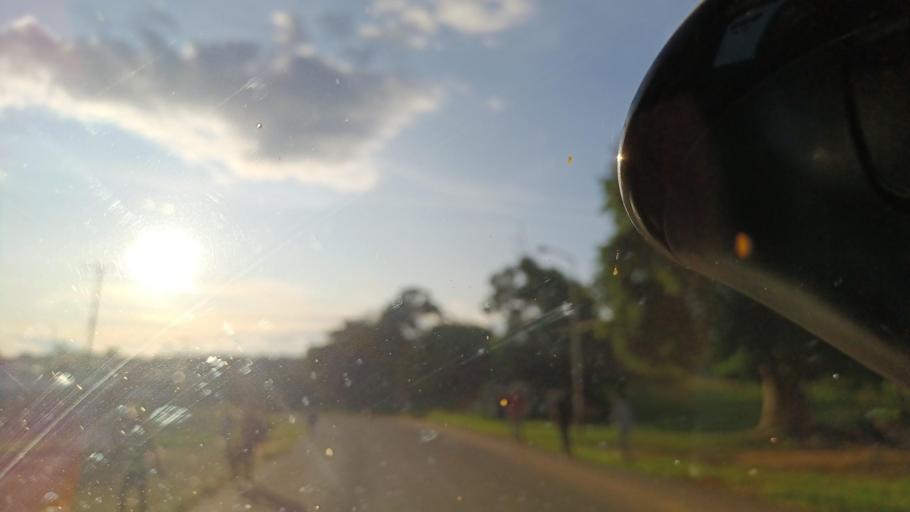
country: ZM
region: North-Western
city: Kasempa
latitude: -13.4587
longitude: 25.8478
